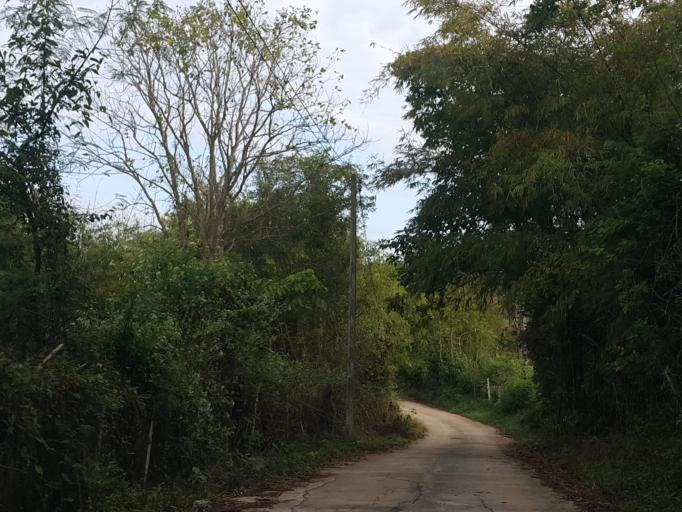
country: TH
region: Lampang
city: Mae Mo
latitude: 18.2518
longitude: 99.6018
